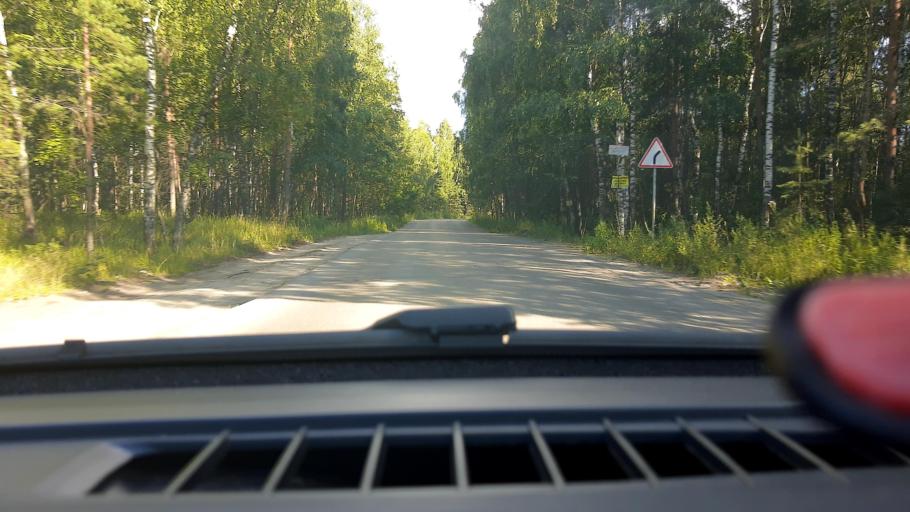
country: RU
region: Nizjnij Novgorod
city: Babino
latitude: 56.3134
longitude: 43.6275
